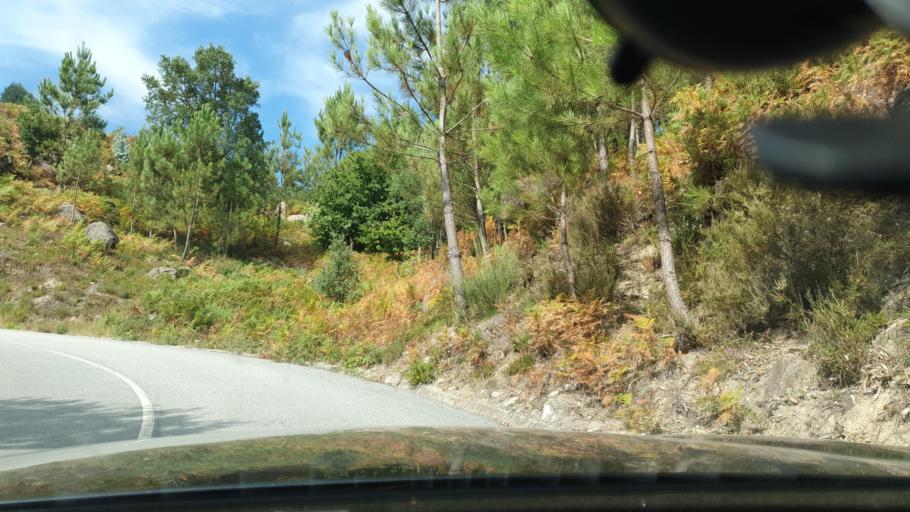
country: PT
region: Braga
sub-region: Vieira do Minho
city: Vieira do Minho
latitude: 41.6992
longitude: -8.0842
